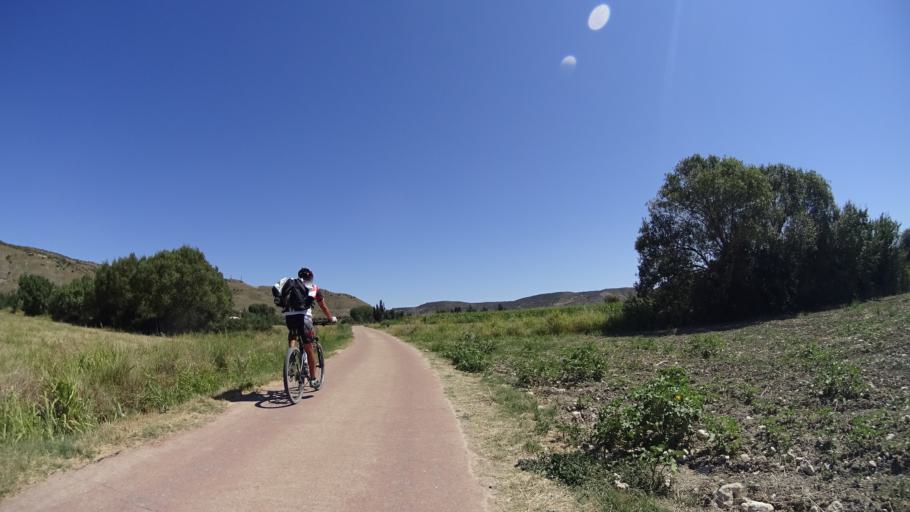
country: ES
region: Madrid
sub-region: Provincia de Madrid
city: Carabana
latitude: 40.2418
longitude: -3.2502
